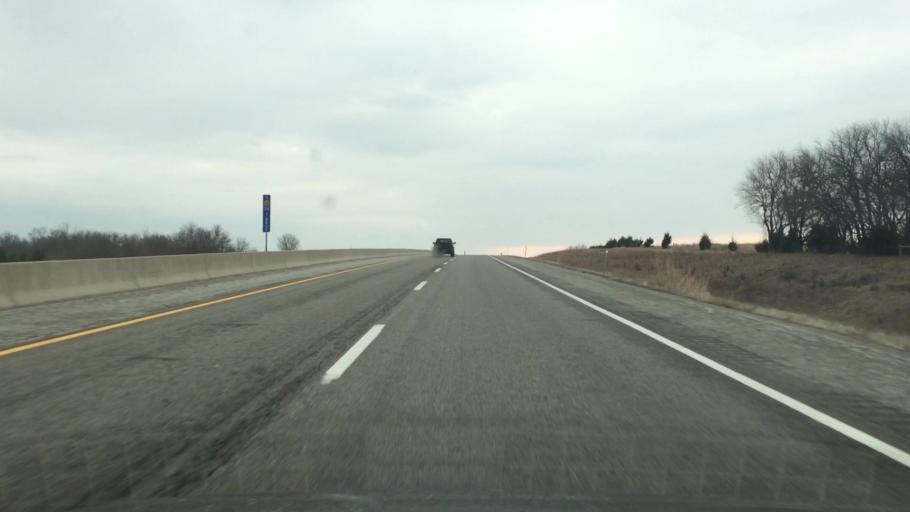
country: US
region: Kansas
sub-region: Shawnee County
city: Auburn
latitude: 38.9084
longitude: -95.7884
